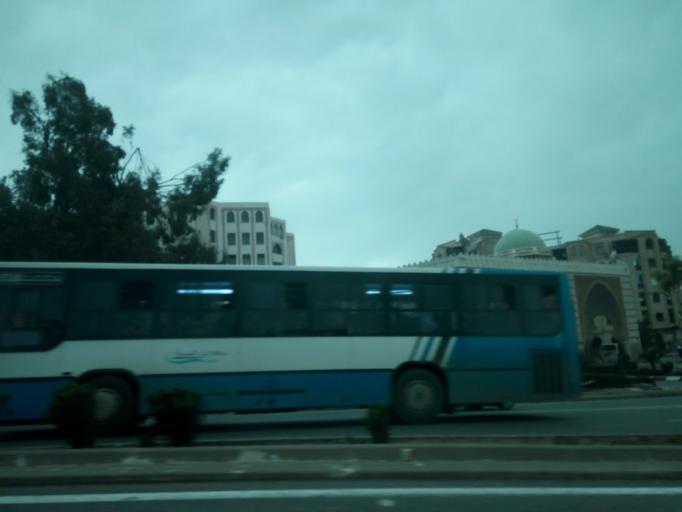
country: DZ
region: Medea
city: Medea
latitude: 36.2651
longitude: 2.7913
